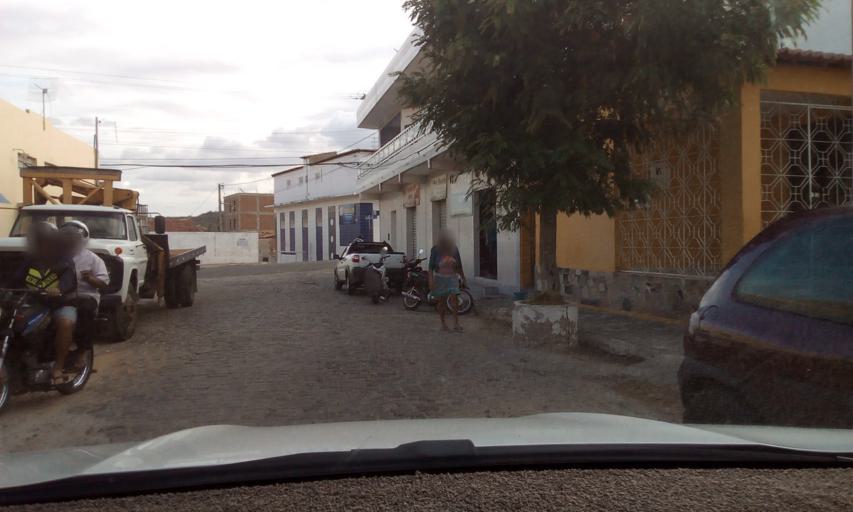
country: BR
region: Paraiba
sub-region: Picui
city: Picui
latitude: -6.5106
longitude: -36.3500
